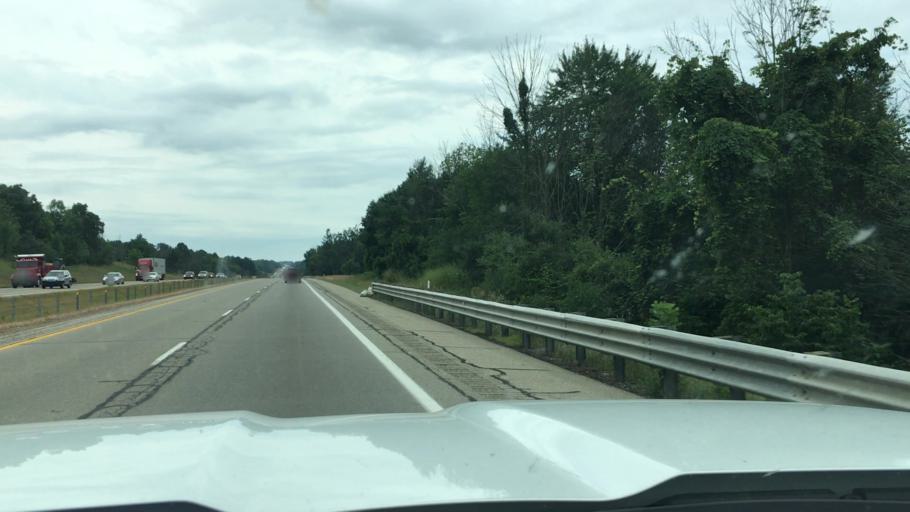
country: US
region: Michigan
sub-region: Allegan County
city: Wayland
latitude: 42.5782
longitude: -85.6628
